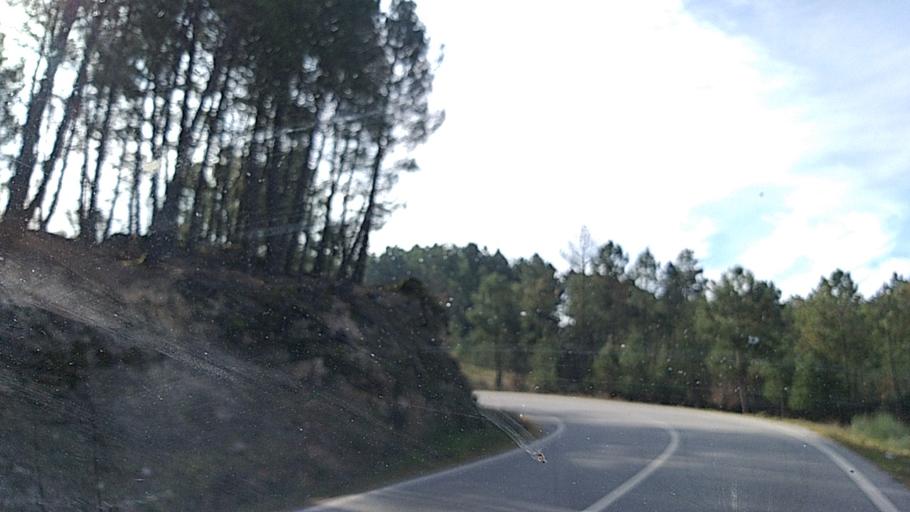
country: PT
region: Guarda
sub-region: Fornos de Algodres
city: Fornos de Algodres
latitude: 40.7086
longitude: -7.5672
